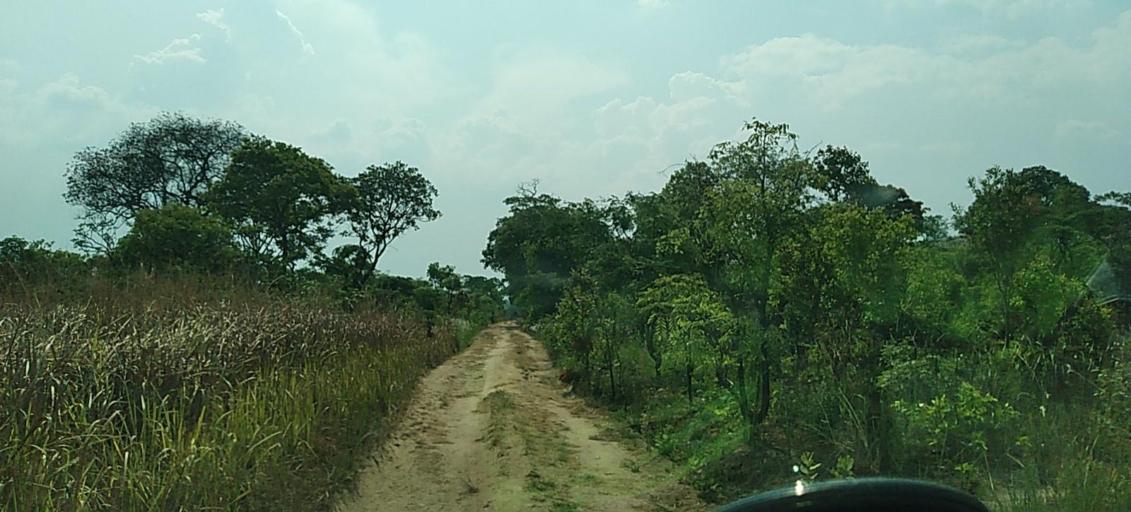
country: ZM
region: North-Western
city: Solwezi
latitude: -12.0934
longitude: 26.2876
